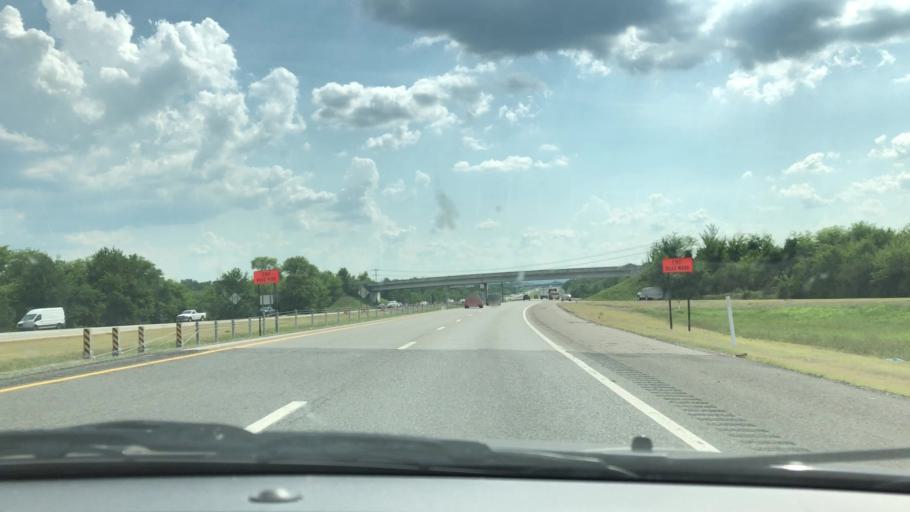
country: US
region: Tennessee
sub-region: Rutherford County
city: Murfreesboro
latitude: 35.8821
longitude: -86.4794
